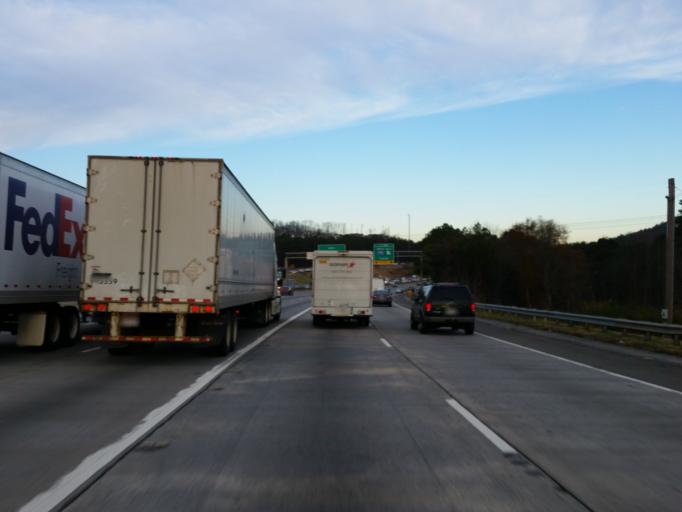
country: US
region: Georgia
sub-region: Cobb County
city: Marietta
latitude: 33.9947
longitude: -84.5571
